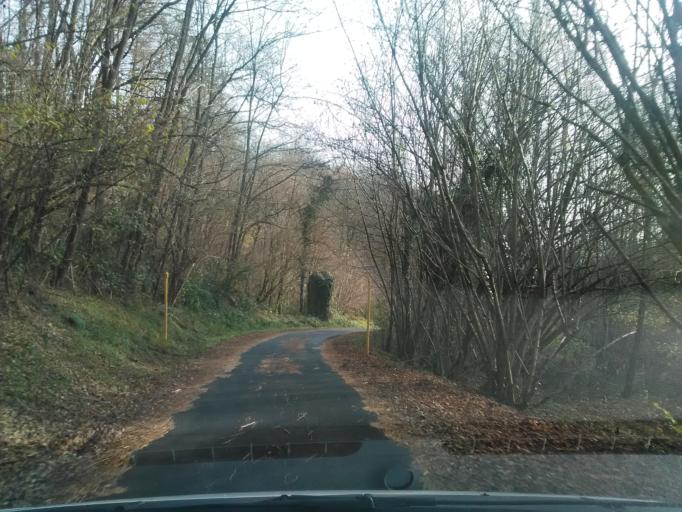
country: IT
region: Piedmont
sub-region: Provincia di Vercelli
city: Guardabosone
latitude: 45.7025
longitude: 8.2408
